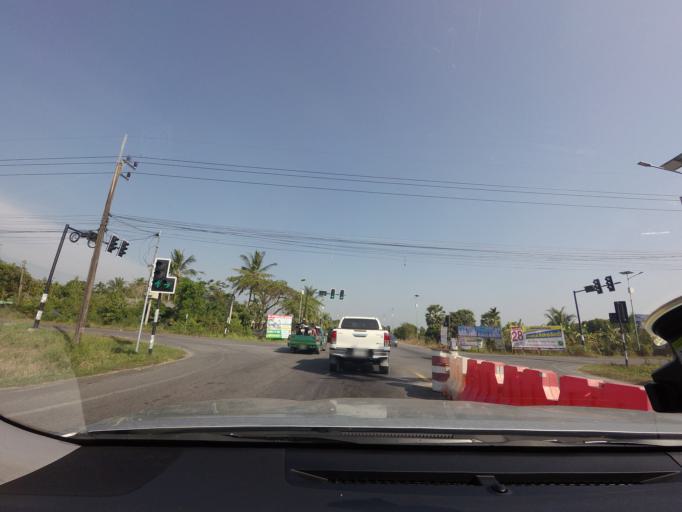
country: TH
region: Nakhon Si Thammarat
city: Nakhon Si Thammarat
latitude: 8.4763
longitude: 99.9788
